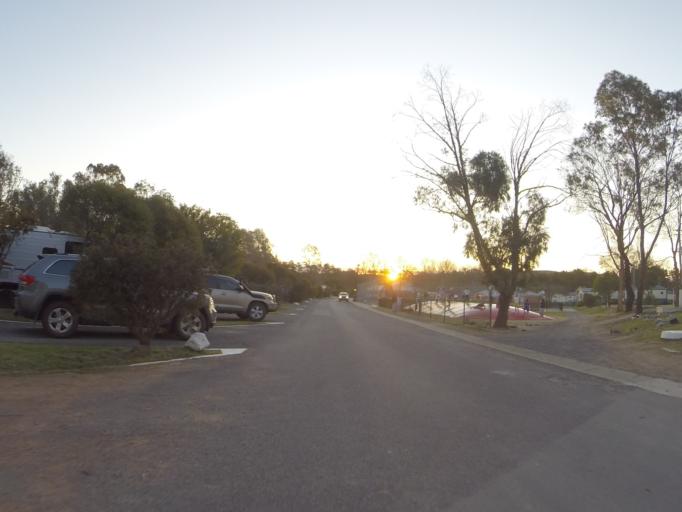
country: AU
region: Australian Capital Territory
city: Kaleen
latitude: -35.1984
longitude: 149.2266
